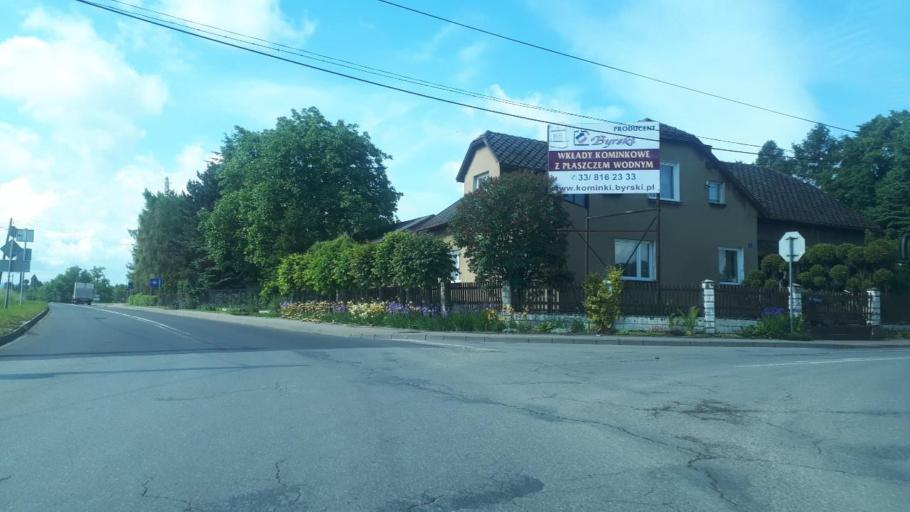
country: PL
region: Lesser Poland Voivodeship
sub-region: Powiat oswiecimski
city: Brzeszcze
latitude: 49.9581
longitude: 19.1375
